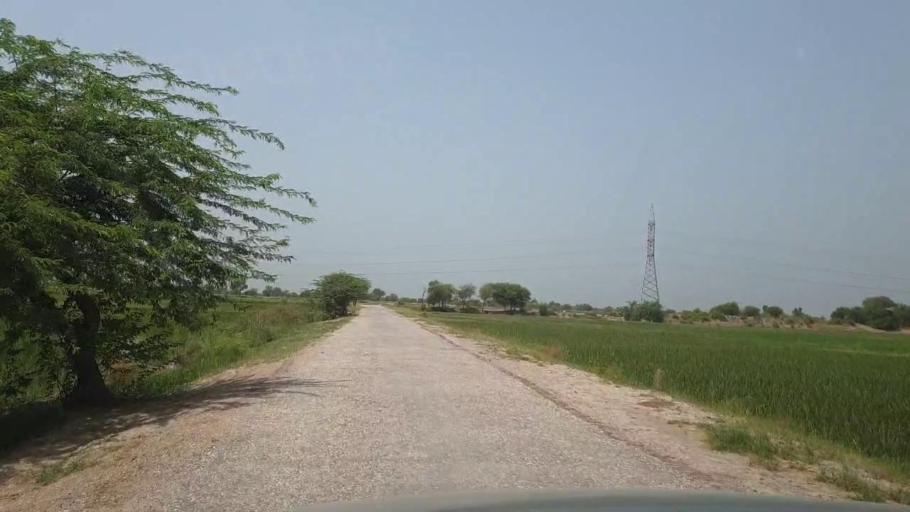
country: PK
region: Sindh
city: Garhi Yasin
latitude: 27.8723
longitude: 68.4485
